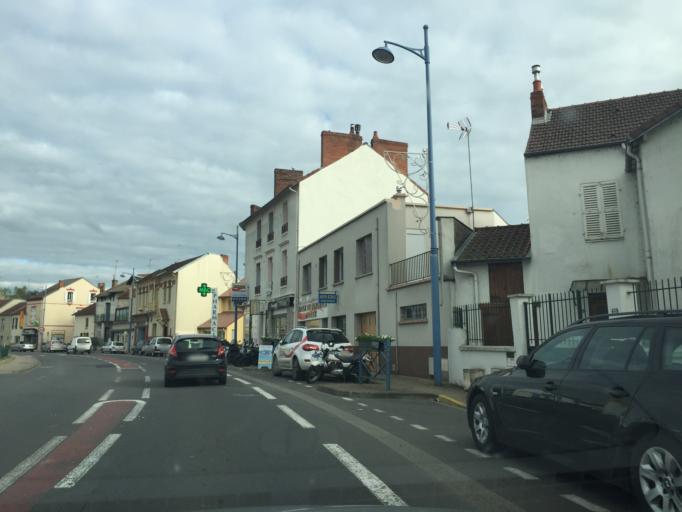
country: FR
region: Auvergne
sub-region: Departement de l'Allier
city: Bellerive-sur-Allier
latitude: 46.1182
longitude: 3.4083
